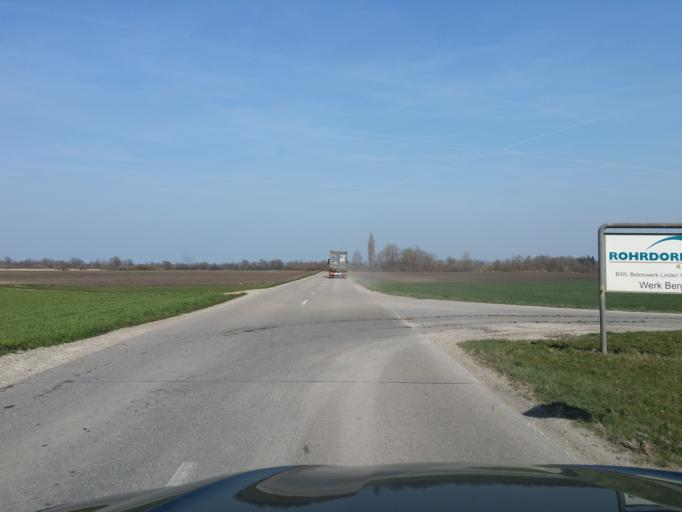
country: DE
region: Bavaria
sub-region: Upper Bavaria
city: Eitting
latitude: 48.3933
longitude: 11.8972
